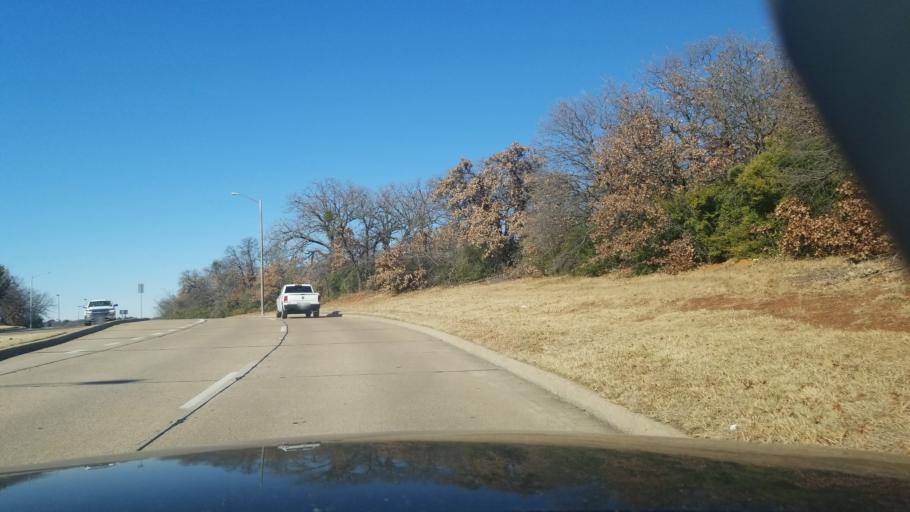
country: US
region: Texas
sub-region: Denton County
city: Denton
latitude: 33.1865
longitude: -97.1009
